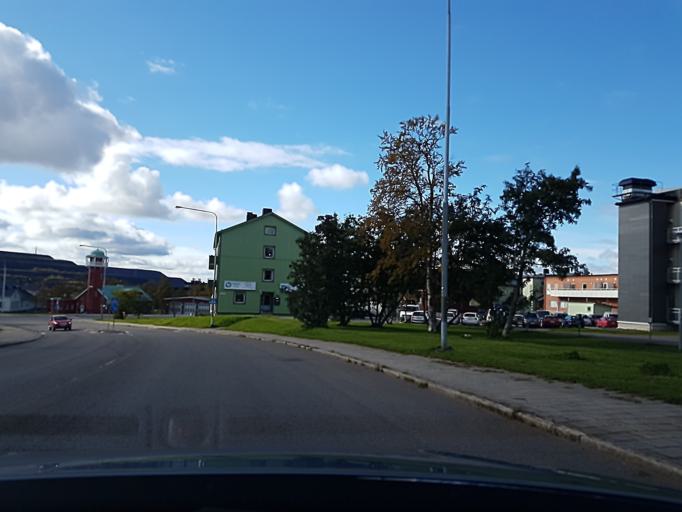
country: SE
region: Norrbotten
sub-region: Kiruna Kommun
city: Kiruna
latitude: 67.8530
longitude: 20.2313
